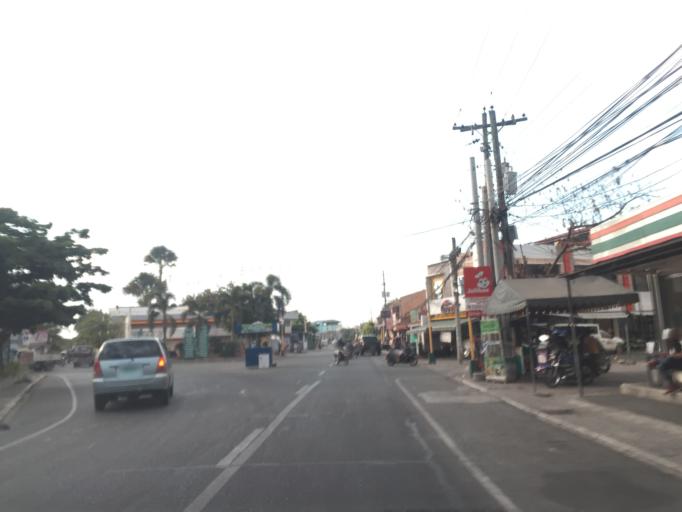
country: PH
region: Ilocos
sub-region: Province of Pangasinan
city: Bolingit
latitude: 15.9335
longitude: 120.3476
